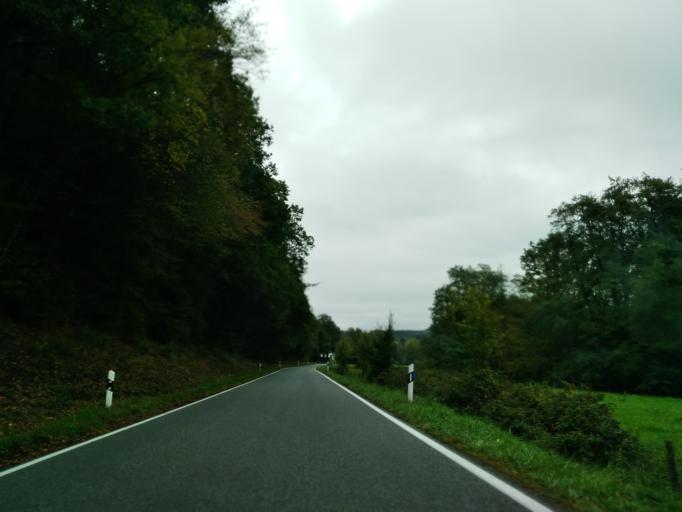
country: DE
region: Rheinland-Pfalz
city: Windhagen
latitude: 50.6302
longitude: 7.3269
